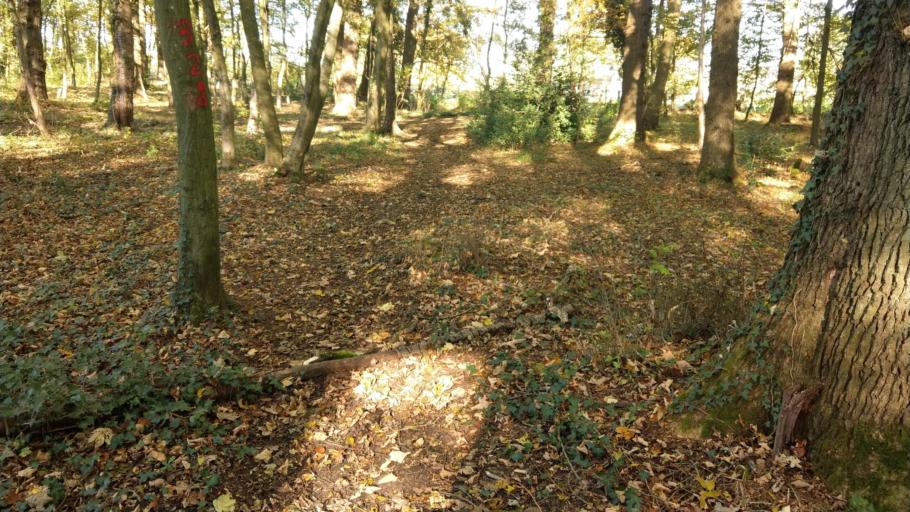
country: BE
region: Wallonia
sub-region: Province de Liege
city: Raeren
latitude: 50.6911
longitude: 6.1356
